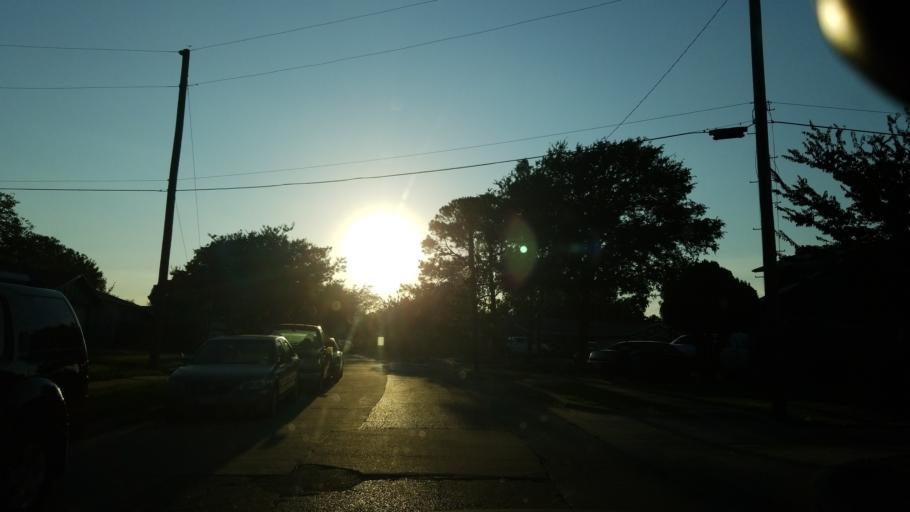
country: US
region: Texas
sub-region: Dallas County
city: Carrollton
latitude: 32.9482
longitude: -96.8836
